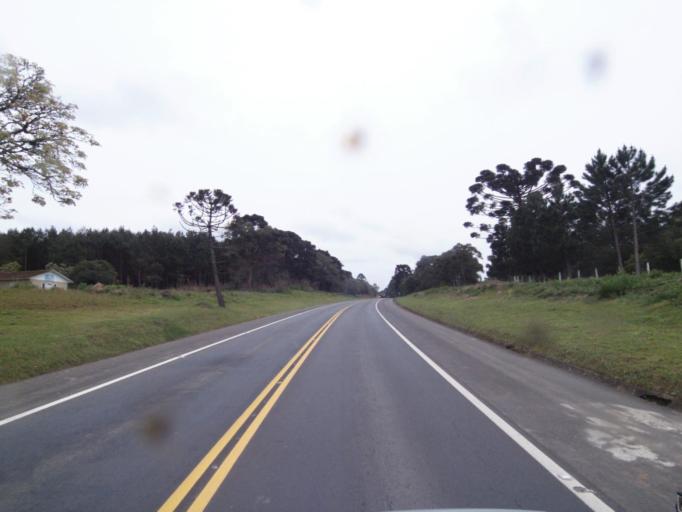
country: BR
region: Parana
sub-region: Irati
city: Irati
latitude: -25.4662
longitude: -50.5359
